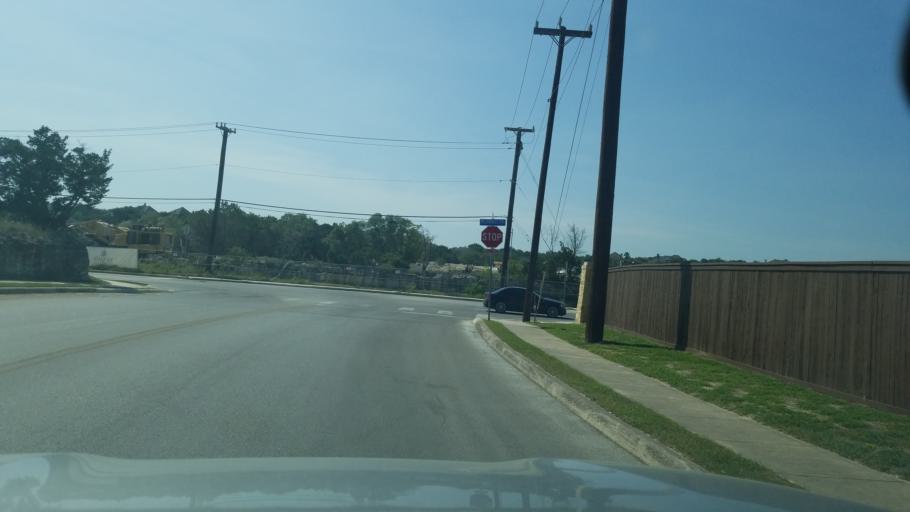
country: US
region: Texas
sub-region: Bexar County
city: Timberwood Park
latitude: 29.6688
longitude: -98.4573
